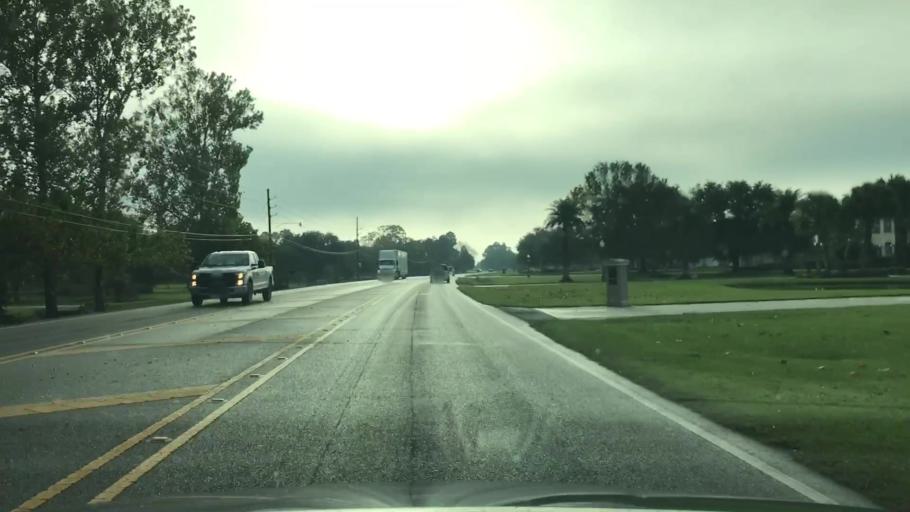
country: US
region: Louisiana
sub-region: Terrebonne Parish
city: Bayou Cane
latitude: 29.6133
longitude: -90.7830
